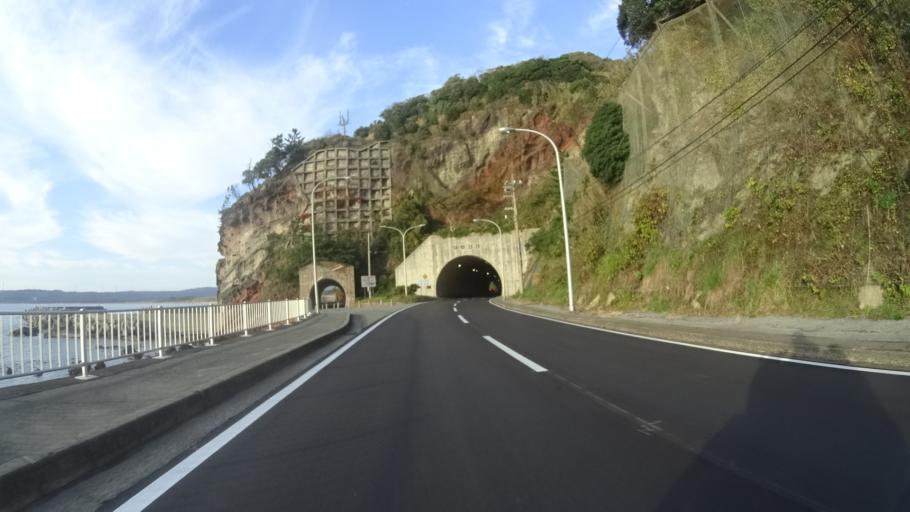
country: JP
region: Ishikawa
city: Nanao
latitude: 37.1316
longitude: 136.7271
